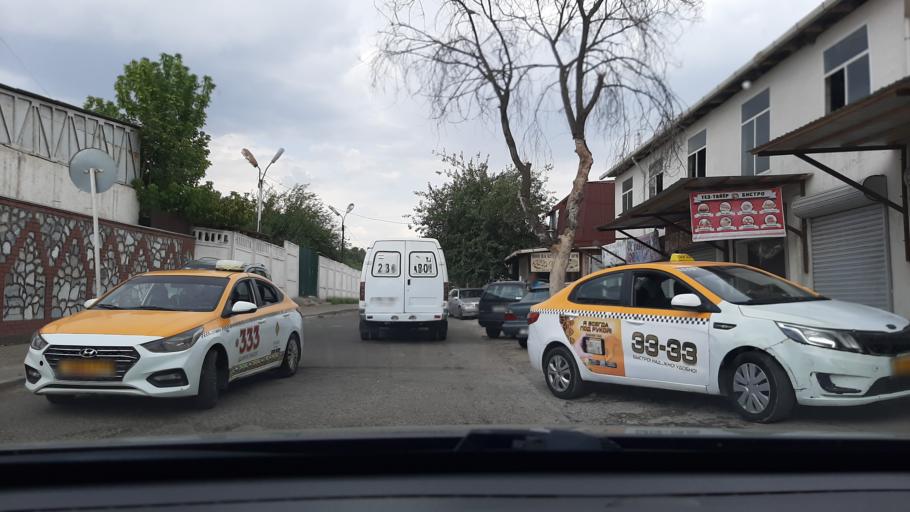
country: TJ
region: Dushanbe
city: Dushanbe
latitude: 38.5706
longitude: 68.7582
